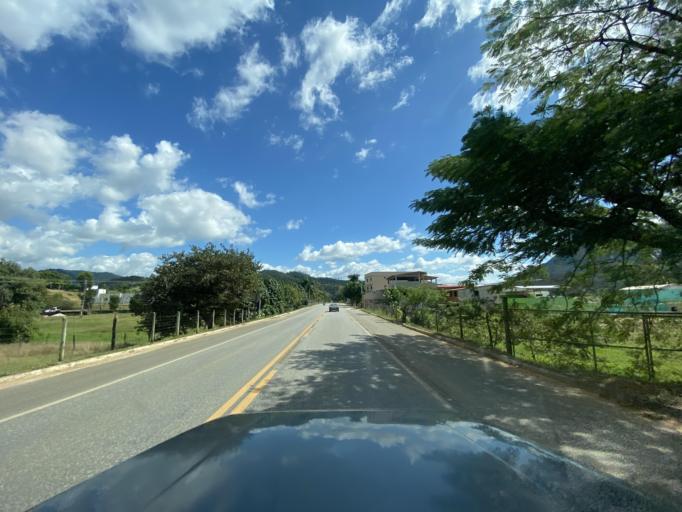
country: BR
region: Espirito Santo
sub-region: Jeronimo Monteiro
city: Jeronimo Monteiro
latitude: -20.7629
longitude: -41.4500
